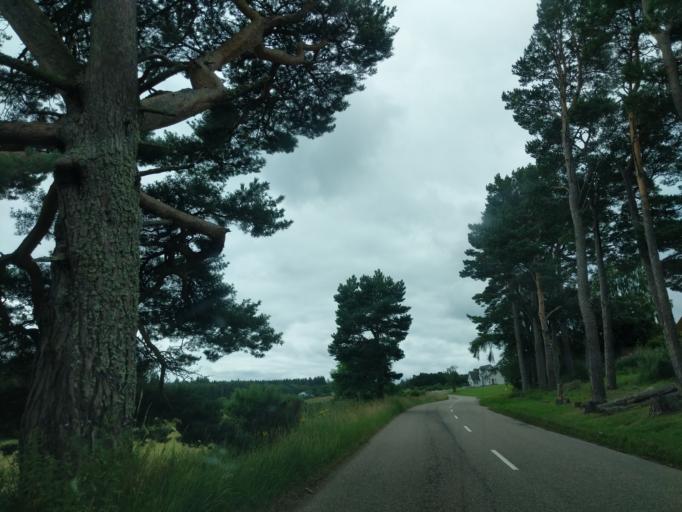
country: GB
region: Scotland
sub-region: Moray
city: Rothes
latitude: 57.4866
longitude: -3.2495
